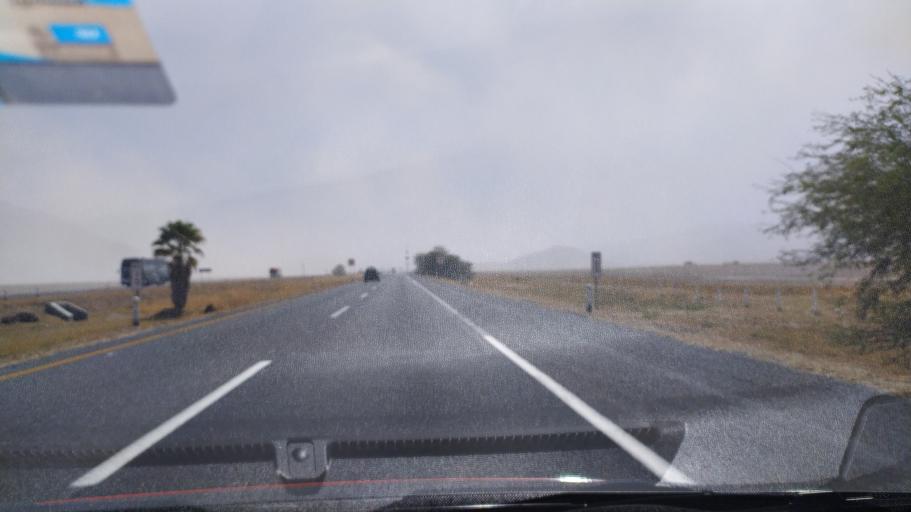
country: MX
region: Jalisco
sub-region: Acatlan de Juarez
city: Villa de los Ninos
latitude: 20.3271
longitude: -103.5676
